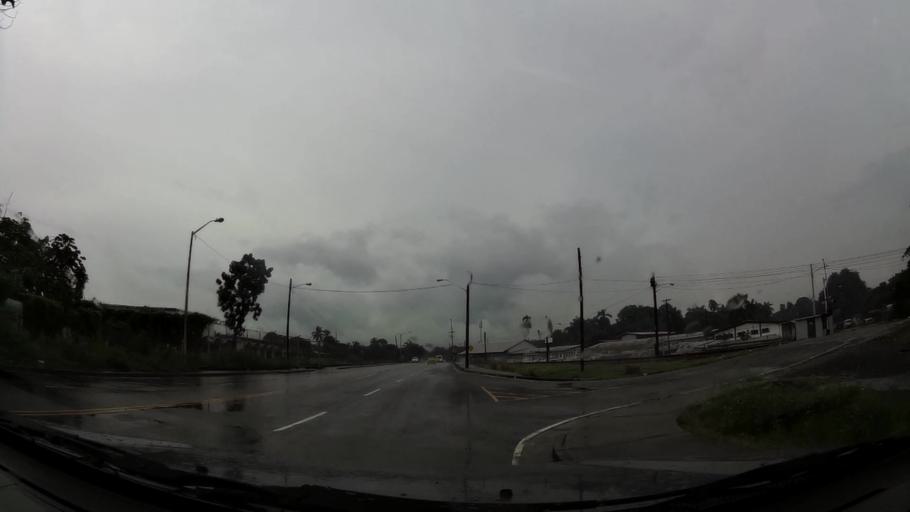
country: PA
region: Colon
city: Arco Iris
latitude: 9.3408
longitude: -79.8949
